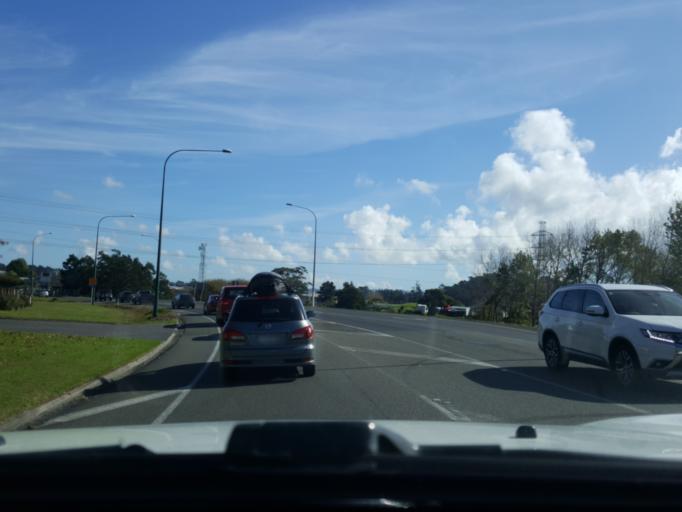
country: NZ
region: Auckland
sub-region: Auckland
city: Muriwai Beach
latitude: -36.7776
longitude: 174.5642
